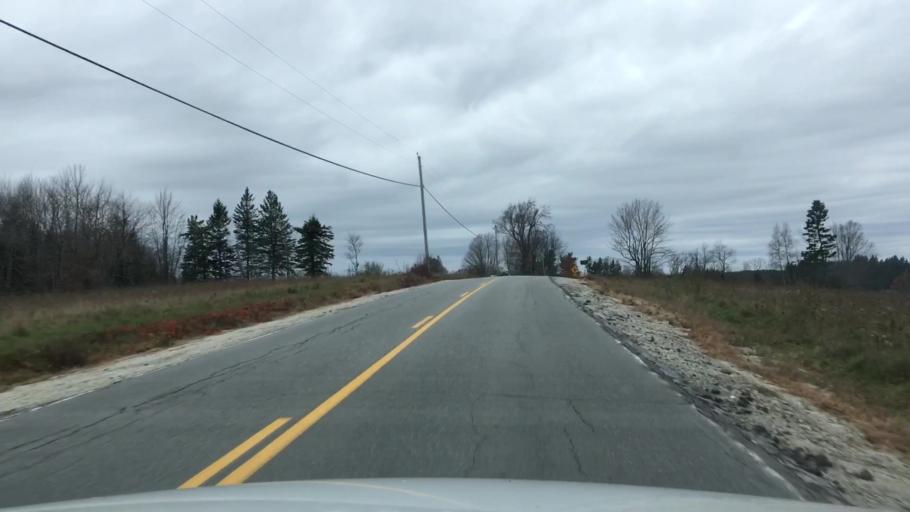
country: US
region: Maine
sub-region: Hancock County
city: Penobscot
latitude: 44.4401
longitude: -68.6351
